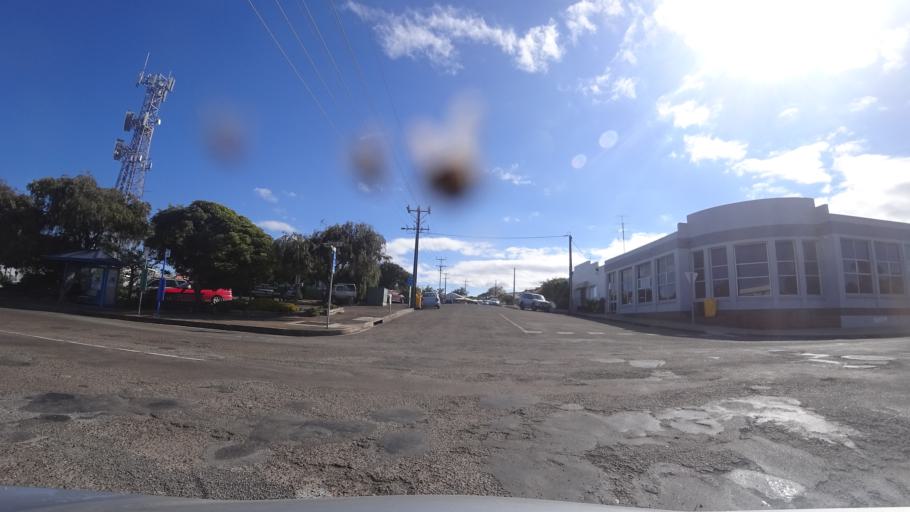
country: AU
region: South Australia
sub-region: Kangaroo Island
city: Kingscote
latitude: -35.6552
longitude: 137.6382
